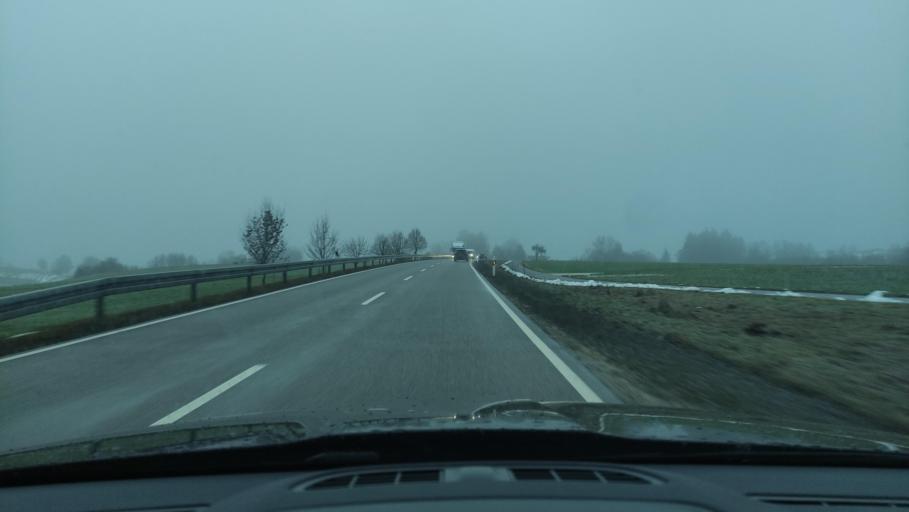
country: DE
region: Bavaria
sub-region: Swabia
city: Weissenhorn
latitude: 48.2944
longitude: 10.1787
